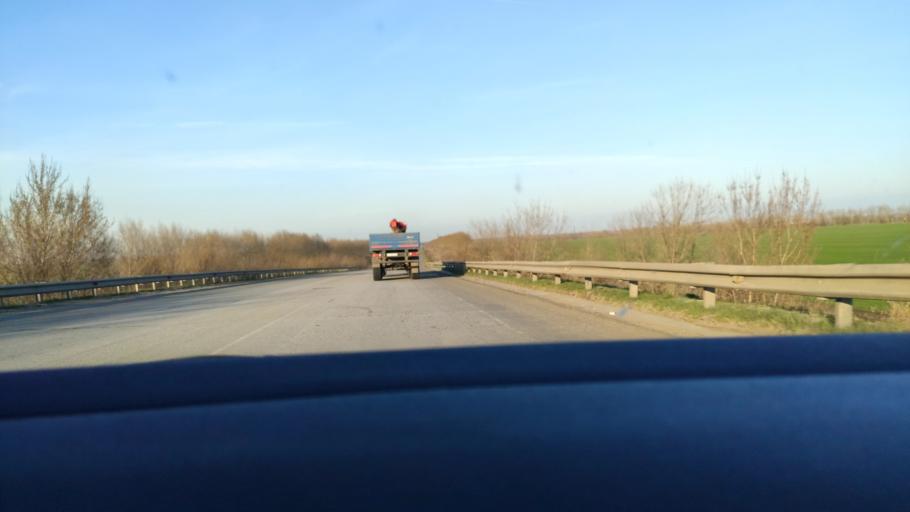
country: RU
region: Voronezj
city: Kolodeznyy
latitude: 51.4108
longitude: 39.2519
